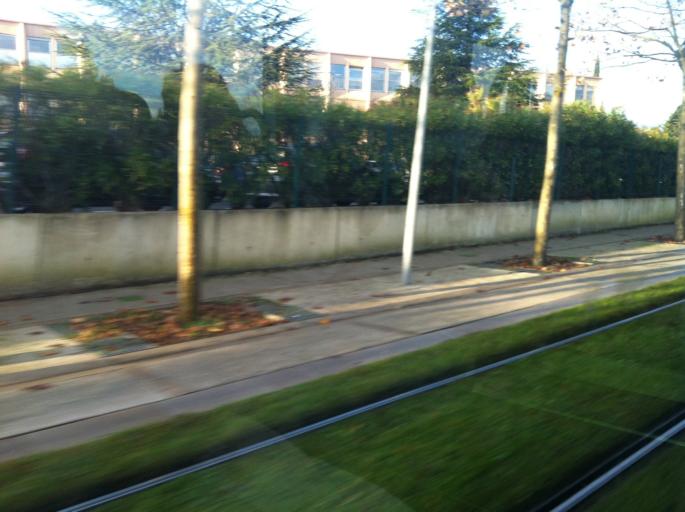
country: FR
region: Languedoc-Roussillon
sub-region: Departement de l'Herault
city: Montpellier
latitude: 43.6307
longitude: 3.8546
